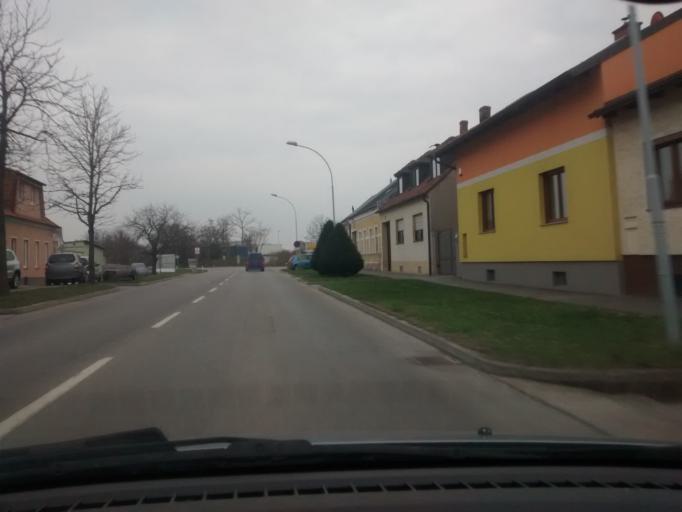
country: AT
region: Lower Austria
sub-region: Politischer Bezirk Wien-Umgebung
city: Fischamend Dorf
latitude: 48.1166
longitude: 16.6051
